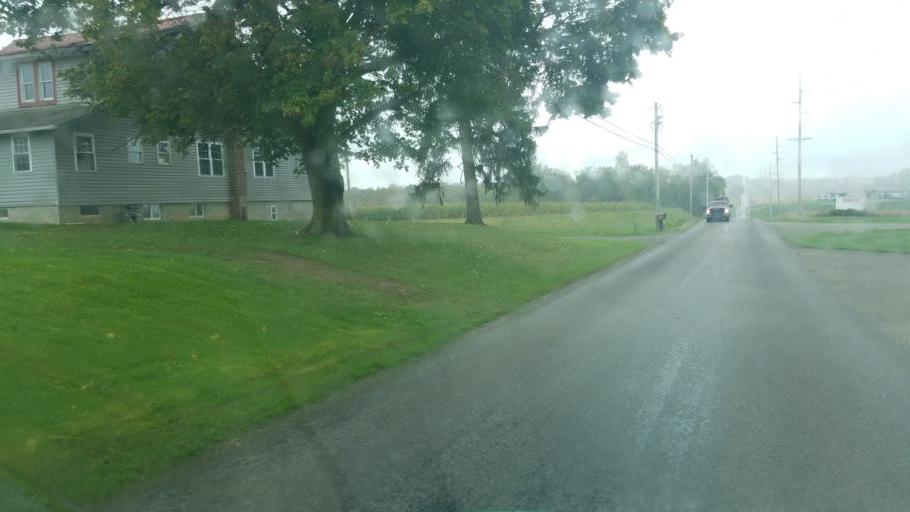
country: US
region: Ohio
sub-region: Holmes County
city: Millersburg
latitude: 40.5916
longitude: -81.8493
